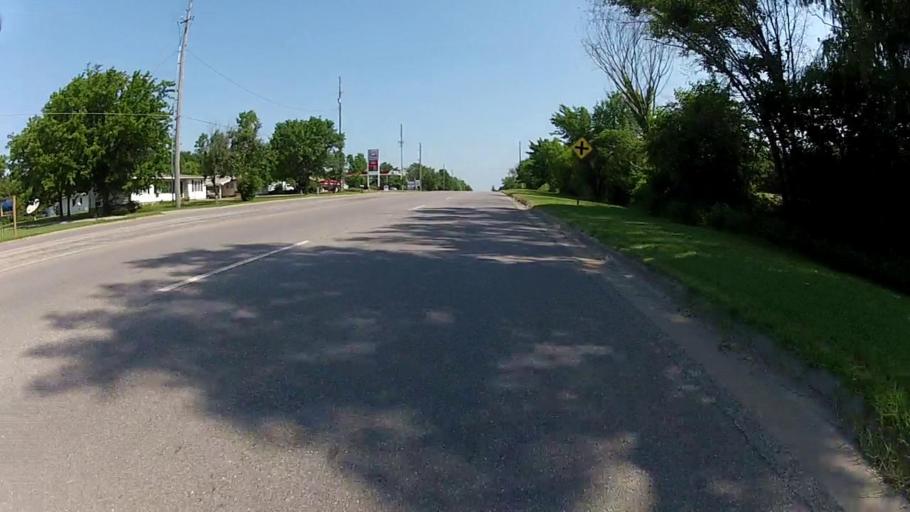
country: US
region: Kansas
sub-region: Montgomery County
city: Independence
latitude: 37.1948
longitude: -95.7106
